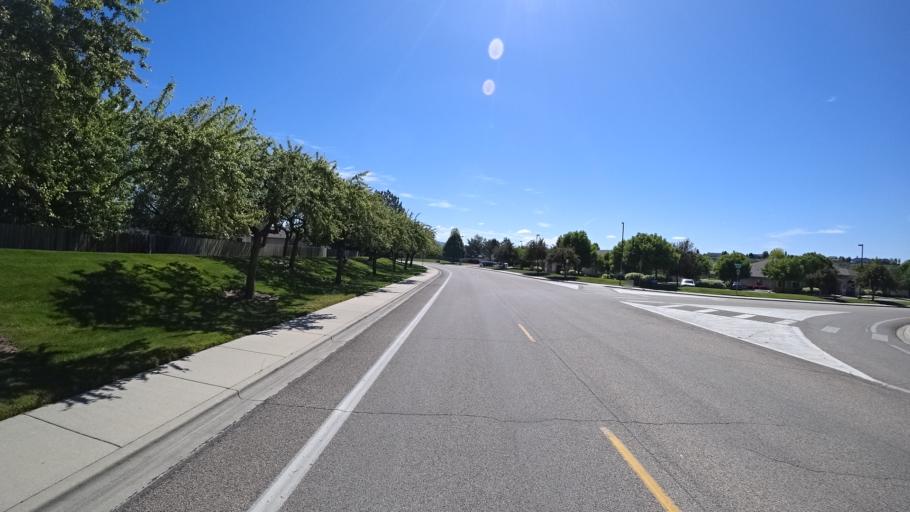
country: US
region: Idaho
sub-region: Ada County
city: Boise
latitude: 43.5493
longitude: -116.1413
